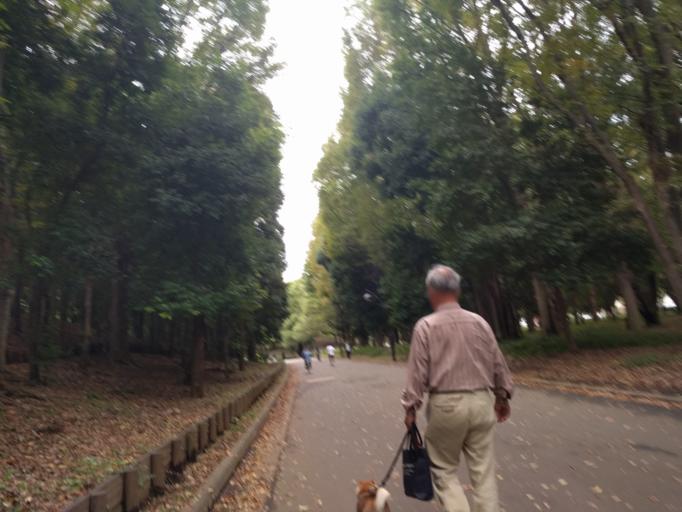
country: JP
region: Saitama
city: Wako
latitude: 35.7657
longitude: 139.6258
